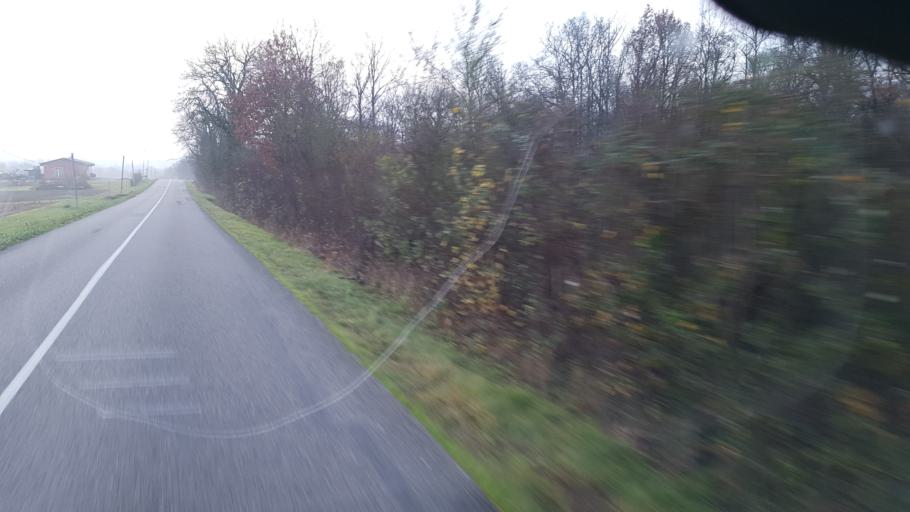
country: FR
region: Midi-Pyrenees
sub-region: Departement du Tarn-et-Garonne
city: Montricoux
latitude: 44.1123
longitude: 1.5932
